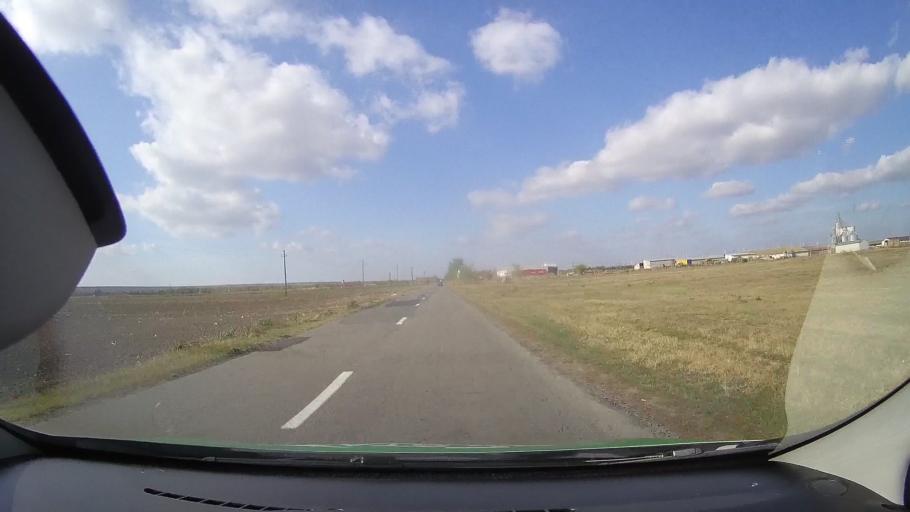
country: RO
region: Constanta
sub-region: Comuna Istria
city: Nuntasi
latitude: 44.5342
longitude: 28.6648
